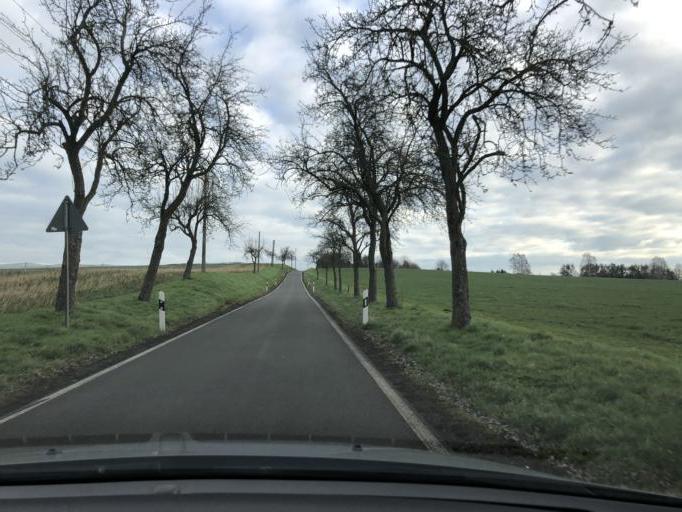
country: DE
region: Saxony
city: Zschadrass
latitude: 51.1982
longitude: 12.8150
